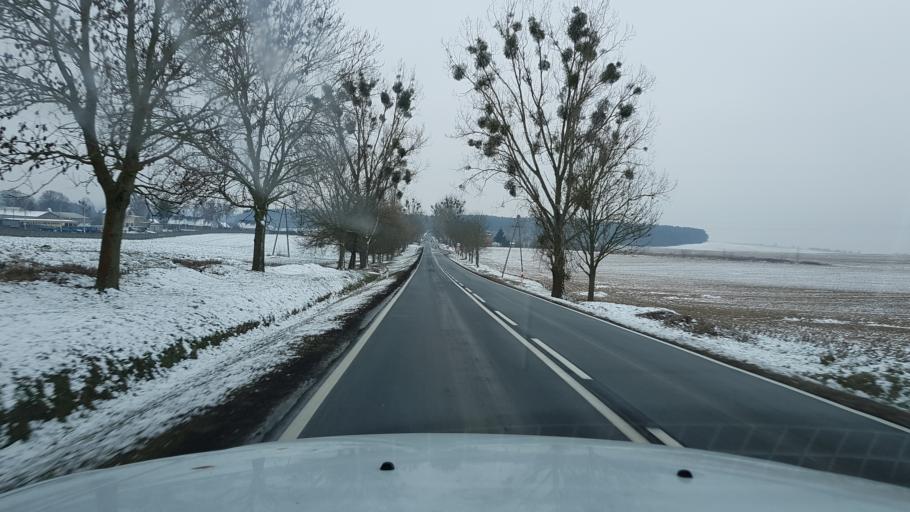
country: PL
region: West Pomeranian Voivodeship
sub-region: Powiat gryfinski
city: Chojna
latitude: 52.9975
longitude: 14.4308
